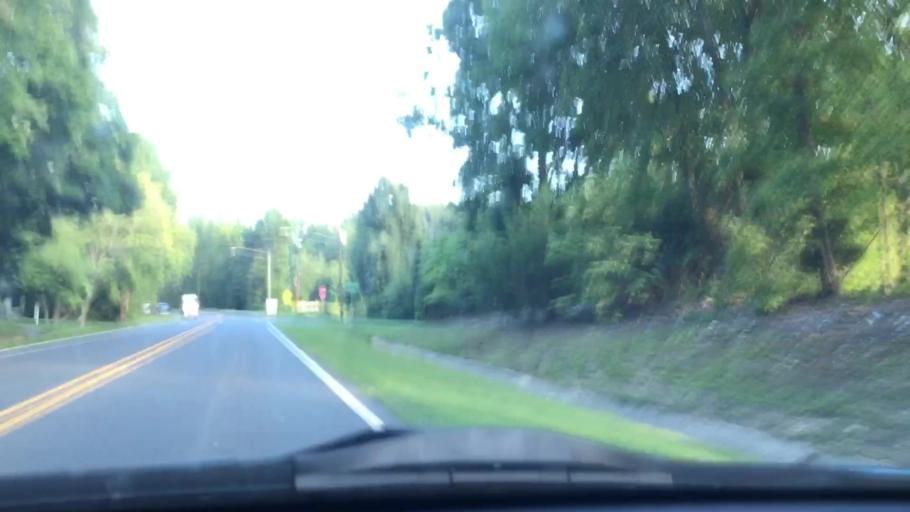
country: US
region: North Carolina
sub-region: Randolph County
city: Asheboro
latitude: 35.7168
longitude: -79.8228
